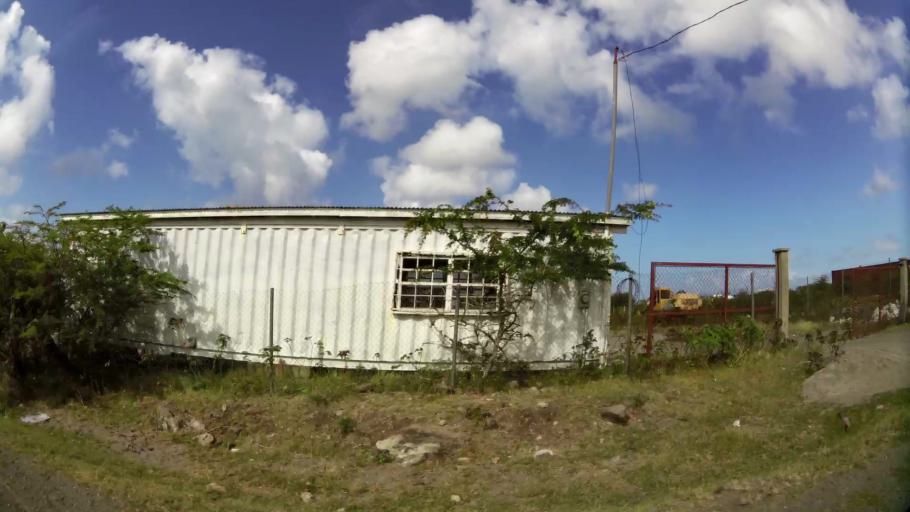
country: KN
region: Saint Paul Charlestown
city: Charlestown
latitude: 17.1175
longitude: -62.6196
